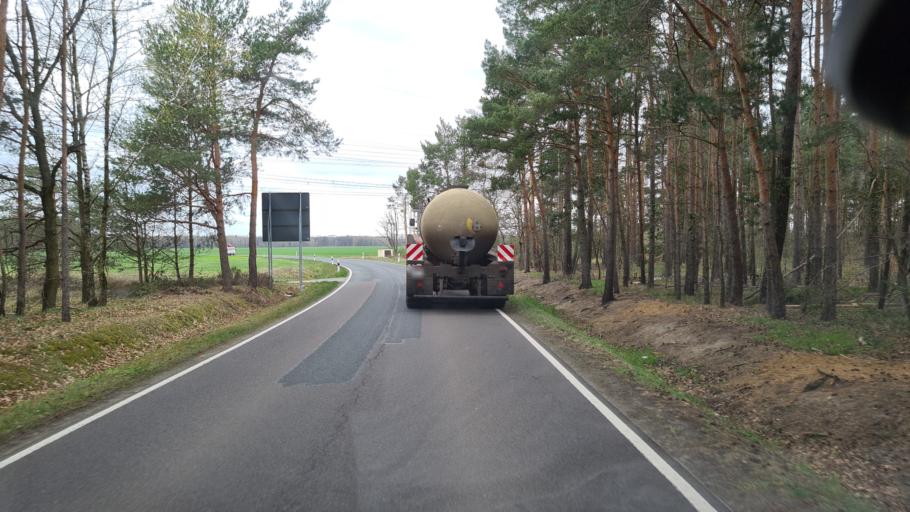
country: DE
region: Brandenburg
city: Hohenbocka
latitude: 51.4546
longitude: 13.9891
